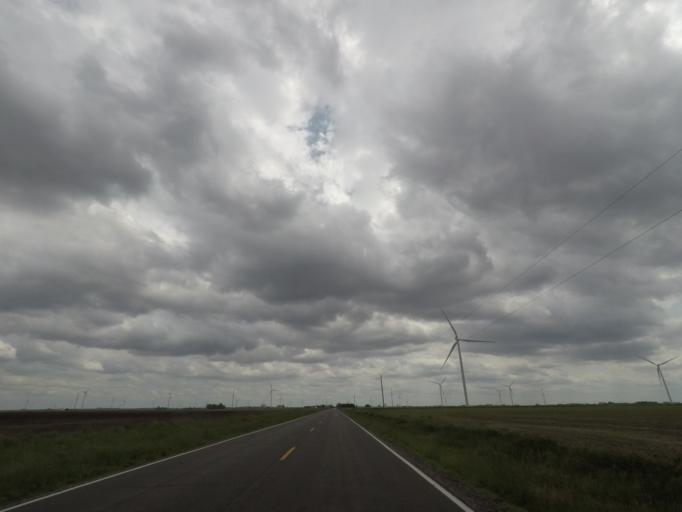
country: US
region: Illinois
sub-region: Macon County
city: Warrensburg
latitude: 40.0161
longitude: -89.0856
